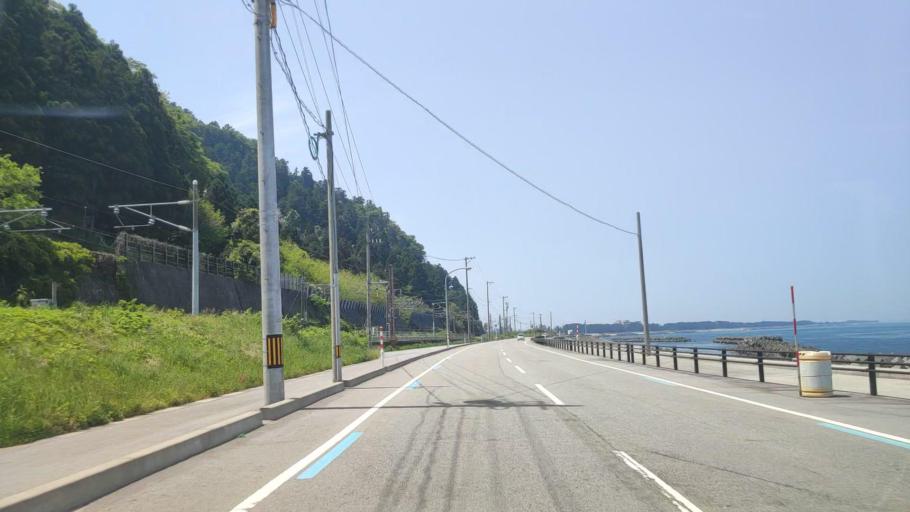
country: JP
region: Toyama
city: Nyuzen
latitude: 36.9693
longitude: 137.5823
